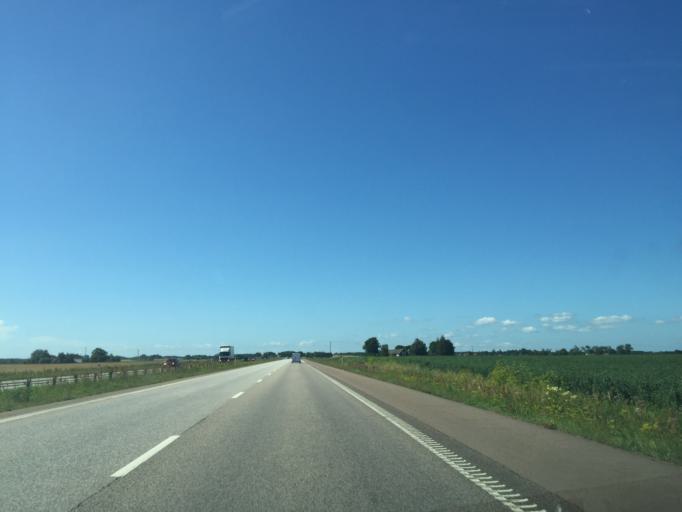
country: SE
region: Skane
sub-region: Angelholms Kommun
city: Strovelstorp
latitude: 56.1238
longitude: 12.8224
